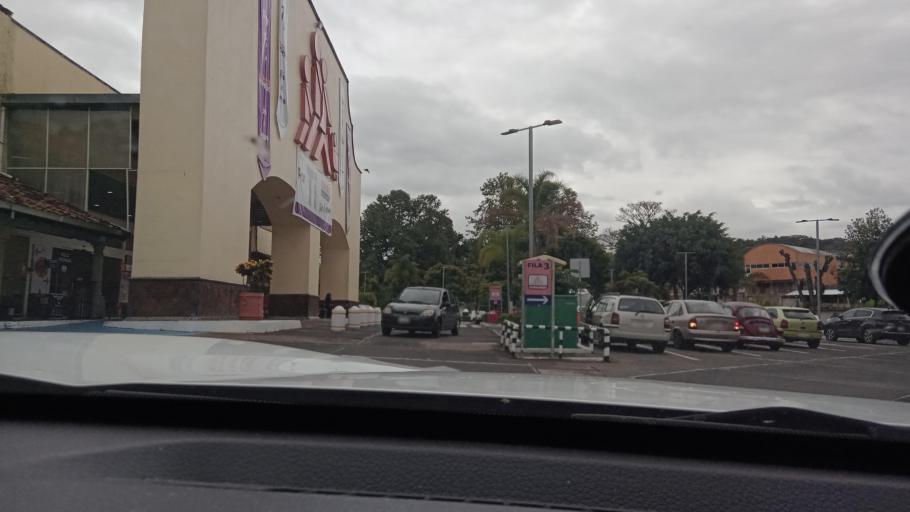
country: MX
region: Veracruz
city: Coatepec
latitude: 19.4488
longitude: -96.9622
